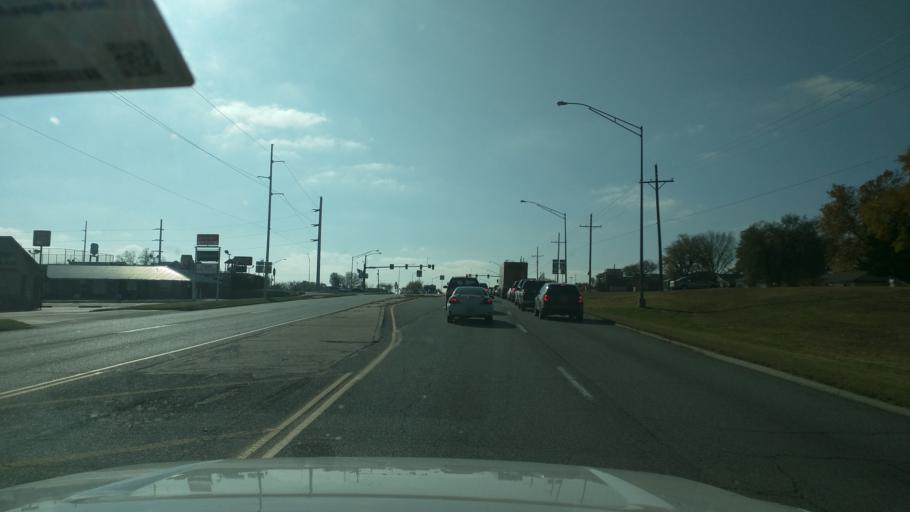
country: US
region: Oklahoma
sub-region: Washington County
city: Bartlesville
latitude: 36.7299
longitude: -95.9352
